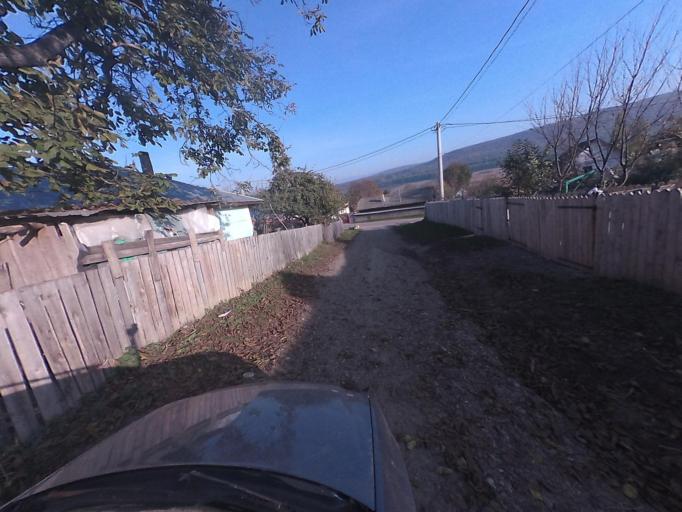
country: RO
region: Vaslui
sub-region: Comuna Bacesti
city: Bacesti
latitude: 46.8231
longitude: 27.2410
